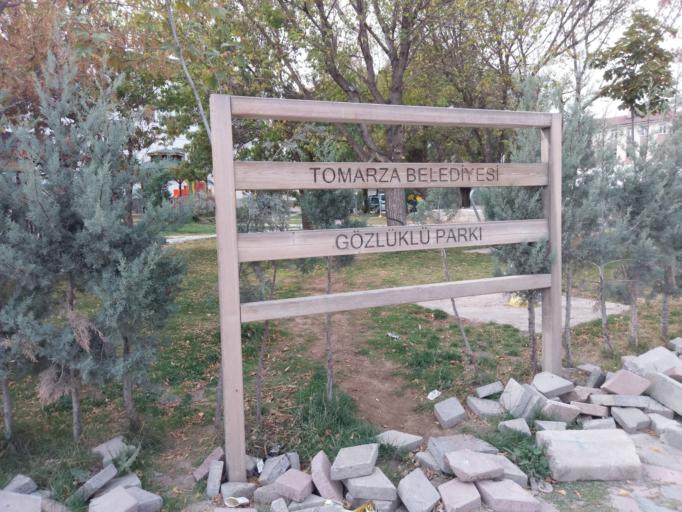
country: TR
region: Kayseri
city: Tomarza
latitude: 38.4478
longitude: 35.8031
